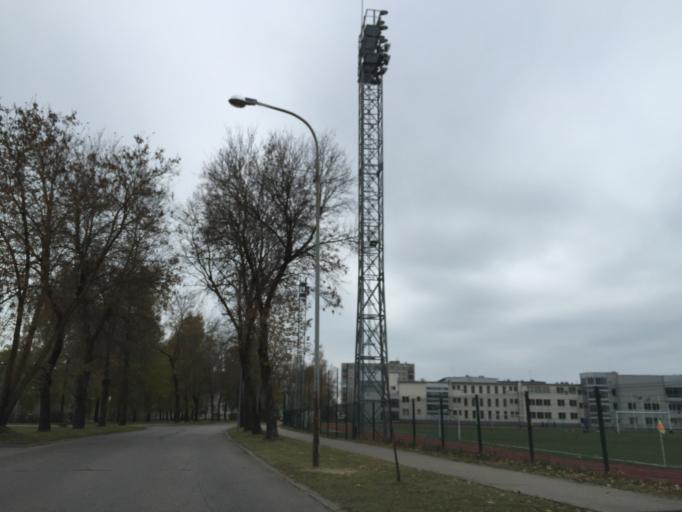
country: LV
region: Olaine
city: Olaine
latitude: 56.7892
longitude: 23.9453
